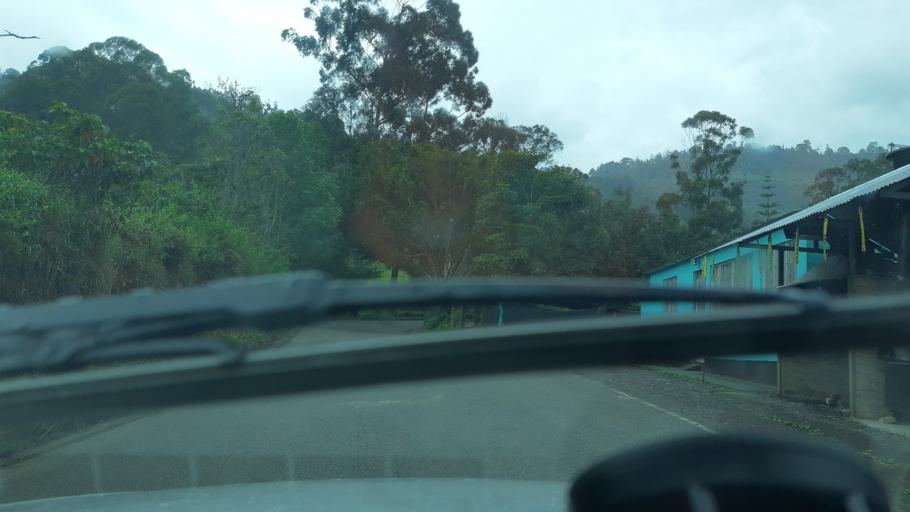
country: CO
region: Boyaca
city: Chinavita
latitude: 5.1696
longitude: -73.3769
